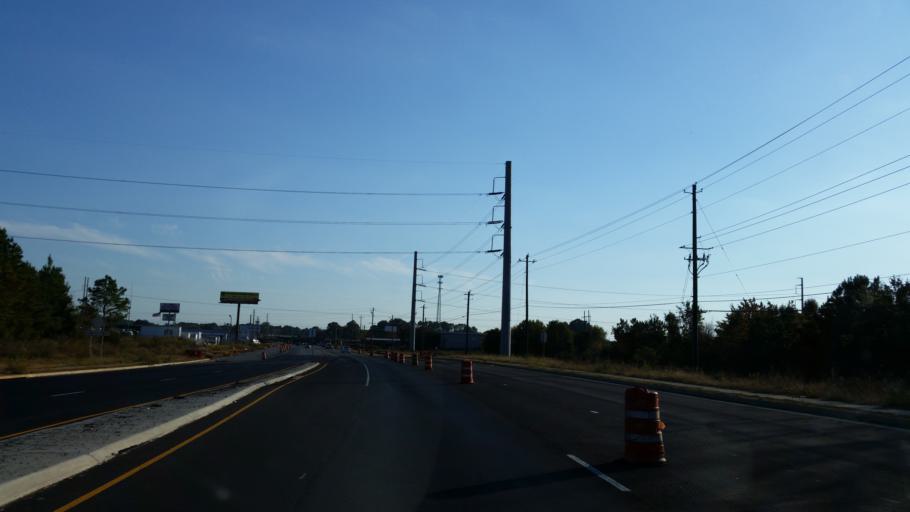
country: US
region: Georgia
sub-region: Bartow County
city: Cartersville
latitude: 34.2067
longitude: -84.7995
